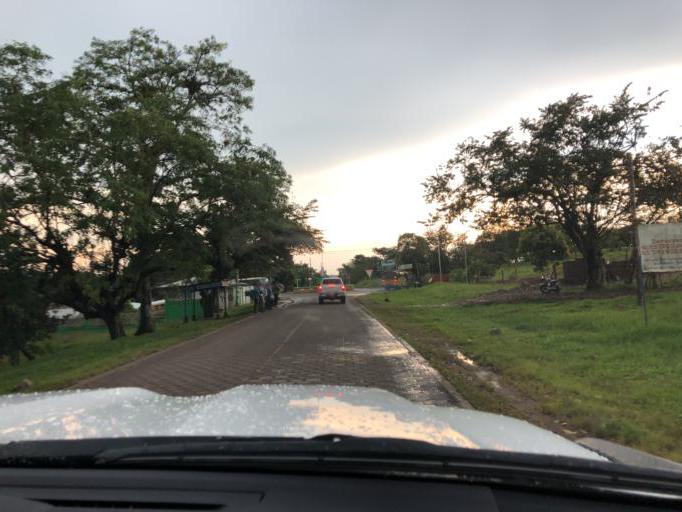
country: NI
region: Chontales
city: La Libertad
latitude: 12.2112
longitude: -85.1776
